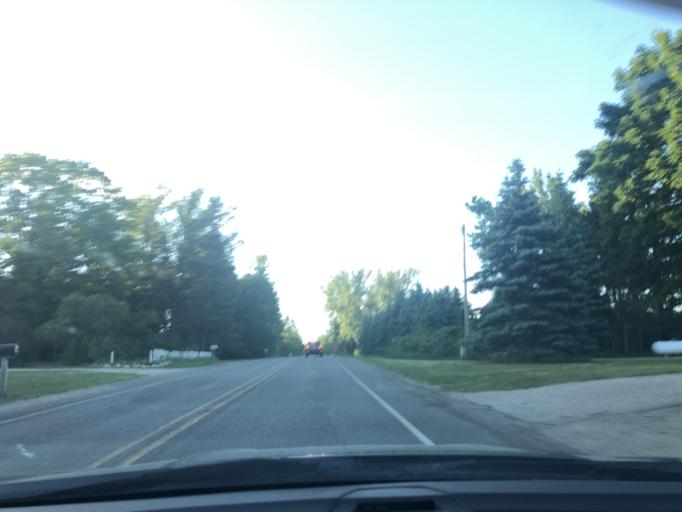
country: US
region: Michigan
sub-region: Missaukee County
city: Lake City
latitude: 44.4494
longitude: -85.0747
